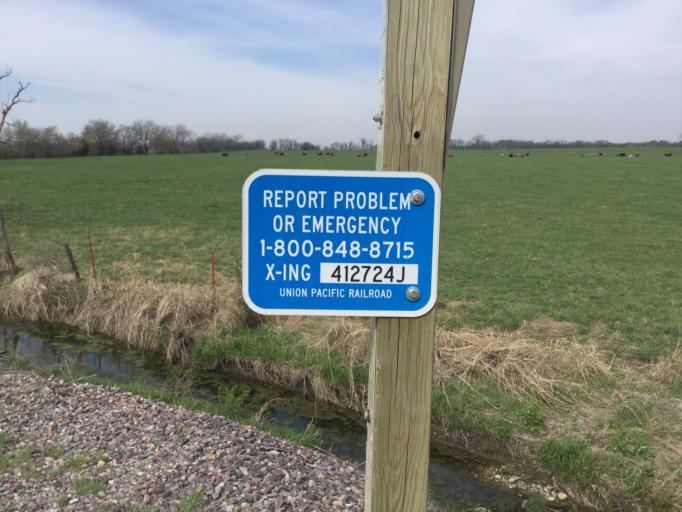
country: US
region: Kansas
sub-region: Neosho County
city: Erie
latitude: 37.4607
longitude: -95.2515
